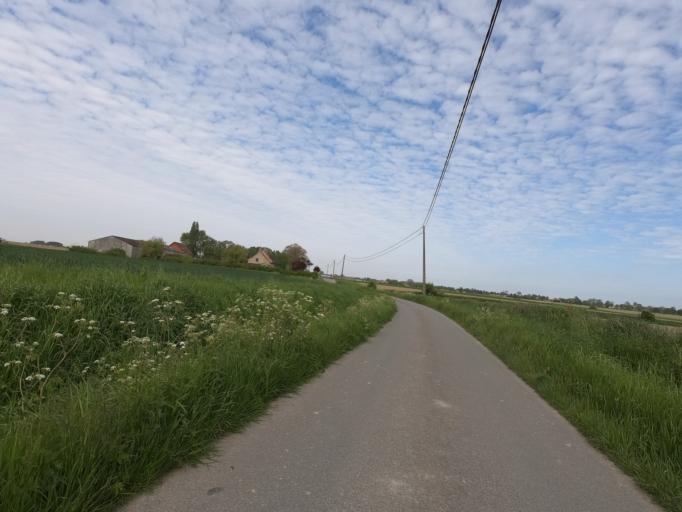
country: BE
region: Flanders
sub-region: Provincie West-Vlaanderen
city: Alveringem
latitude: 50.9664
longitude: 2.7001
